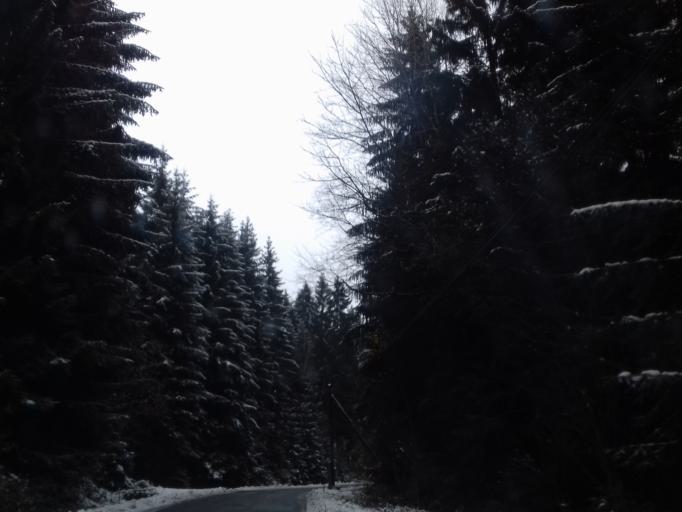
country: CZ
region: Plzensky
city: Postrekov
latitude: 49.4418
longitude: 12.7847
